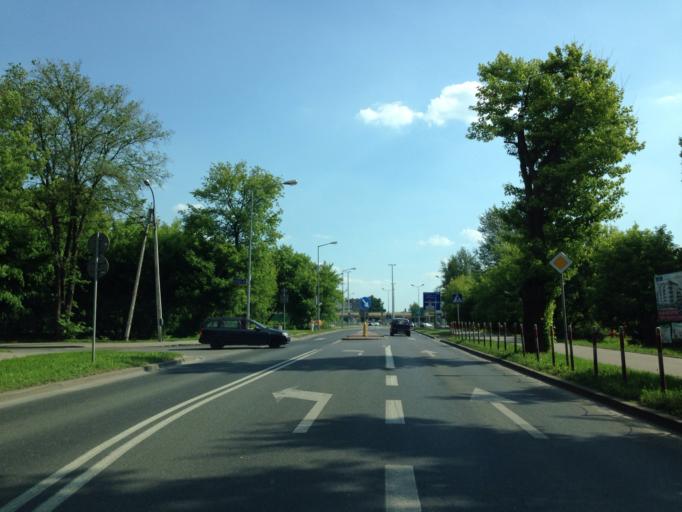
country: PL
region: Masovian Voivodeship
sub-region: Warszawa
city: Bemowo
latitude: 52.2469
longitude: 20.8978
